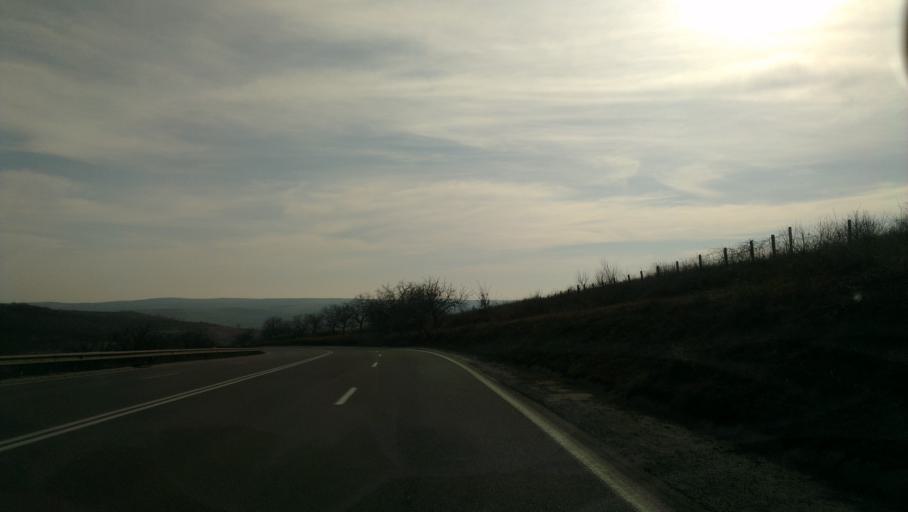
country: MD
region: Laloveni
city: Ialoveni
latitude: 46.9401
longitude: 28.7043
